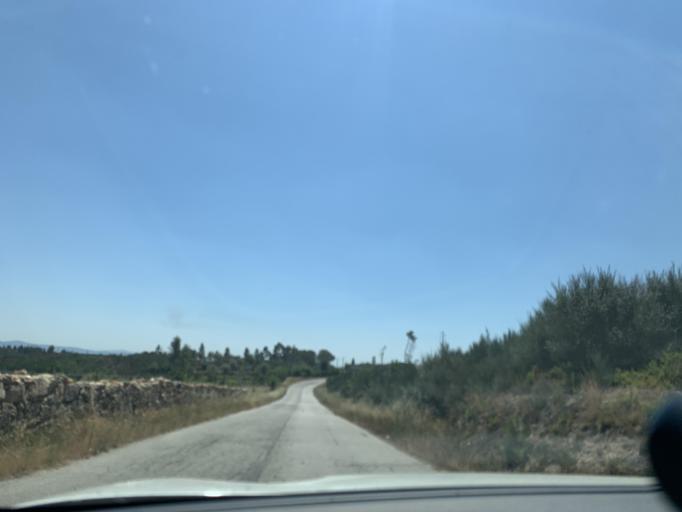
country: PT
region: Viseu
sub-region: Mangualde
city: Mangualde
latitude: 40.5504
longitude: -7.7384
